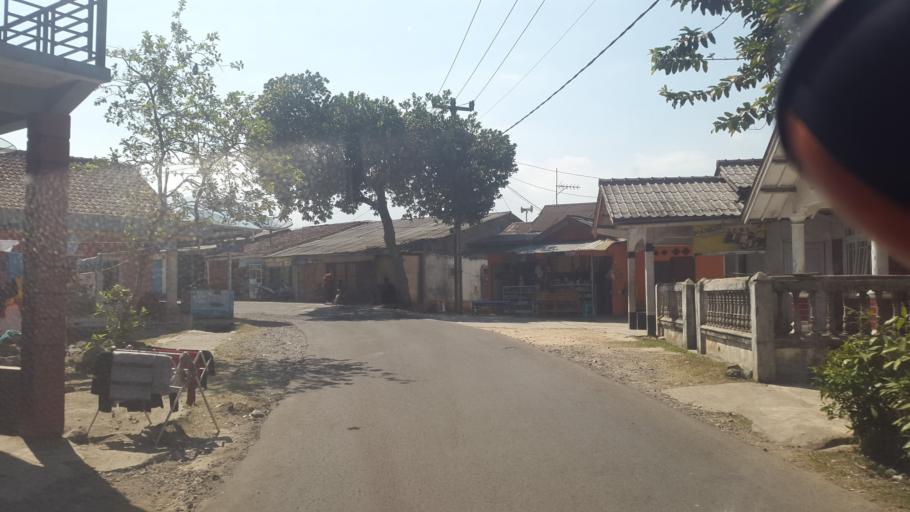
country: ID
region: West Java
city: Cicurug
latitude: -6.8418
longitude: 106.7062
